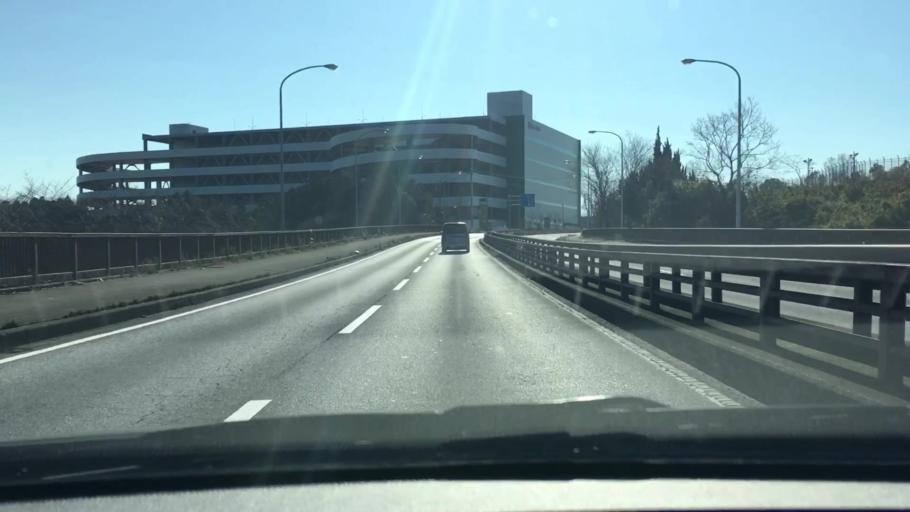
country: JP
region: Chiba
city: Narita
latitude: 35.7432
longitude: 140.4026
